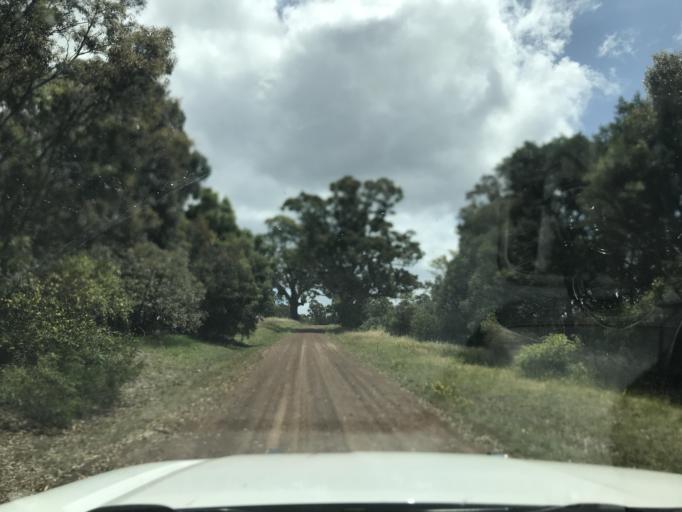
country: AU
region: South Australia
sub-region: Wattle Range
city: Penola
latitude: -37.2979
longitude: 141.4809
